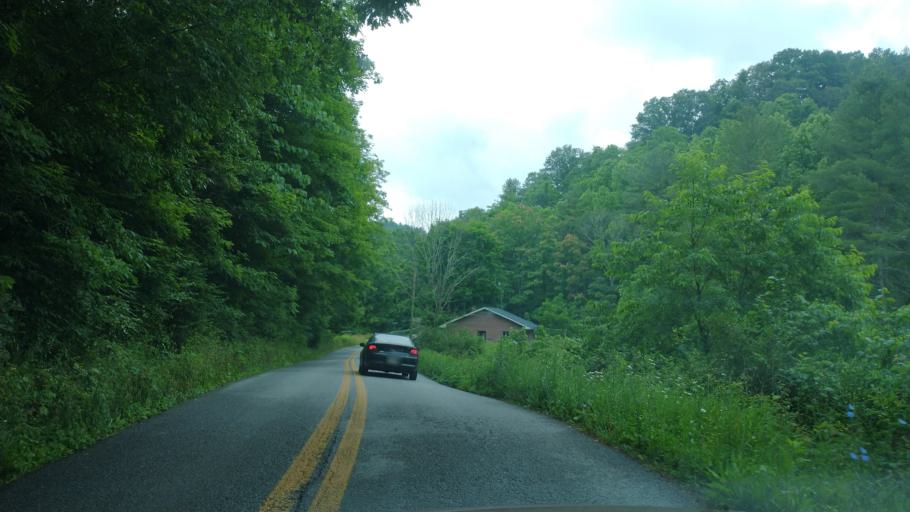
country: US
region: West Virginia
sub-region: Mercer County
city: Athens
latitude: 37.4269
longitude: -80.9949
